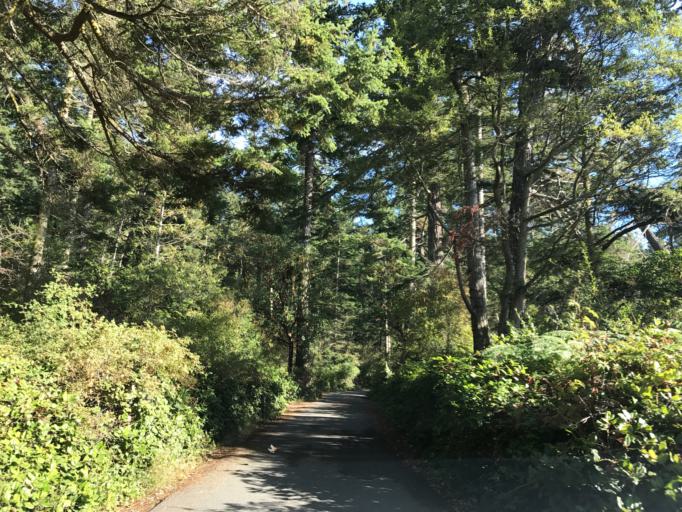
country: US
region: Washington
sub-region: Skagit County
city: Anacortes
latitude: 48.4976
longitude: -122.7007
